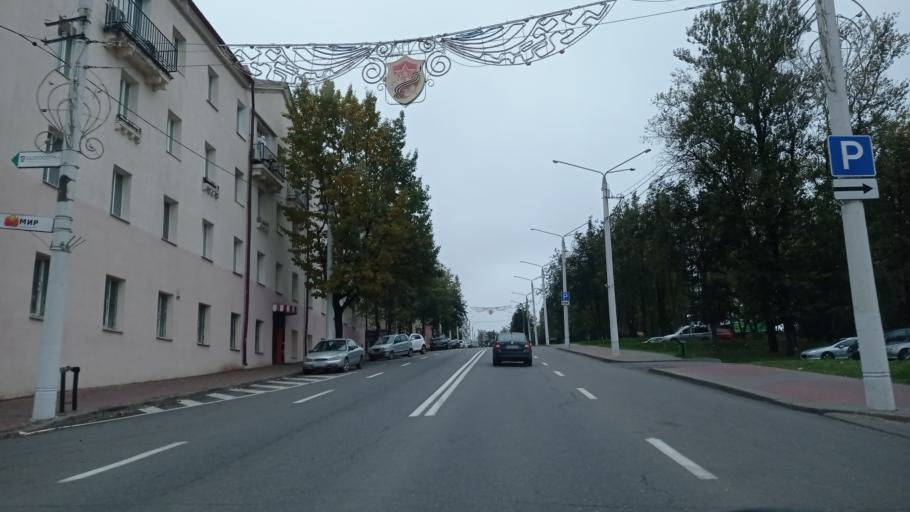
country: BY
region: Vitebsk
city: Vitebsk
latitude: 55.1875
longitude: 30.2015
